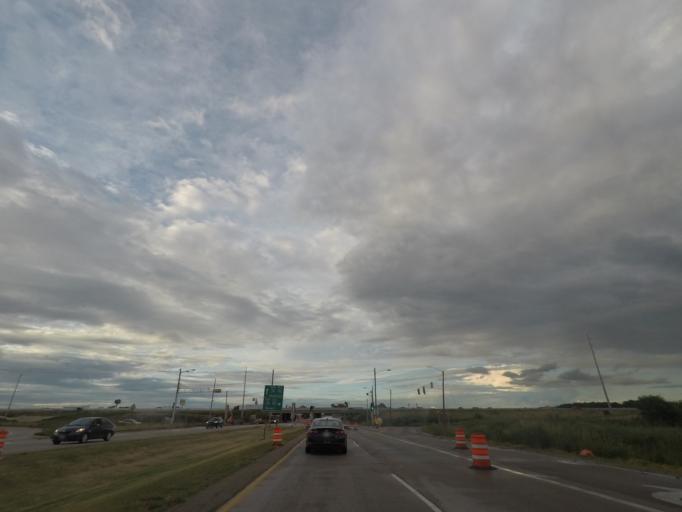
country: US
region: Wisconsin
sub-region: Rock County
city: Janesville
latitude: 42.7240
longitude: -88.9941
